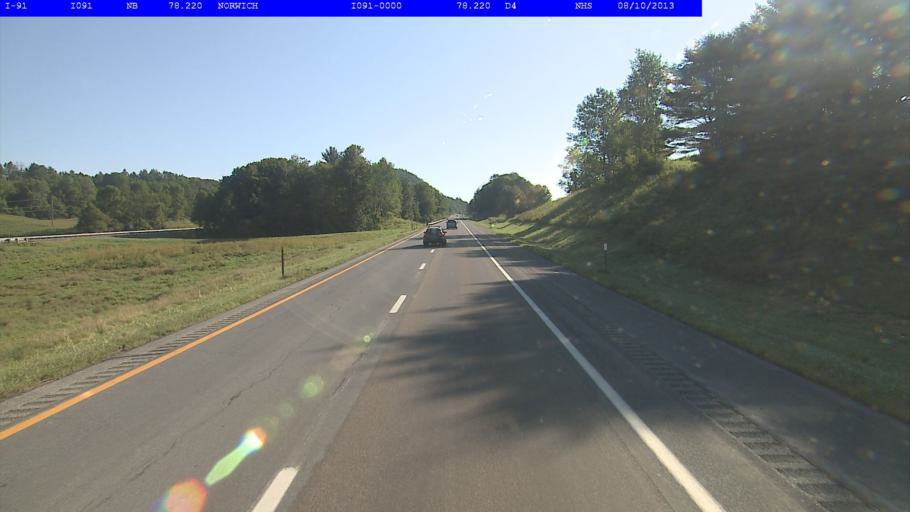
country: US
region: New Hampshire
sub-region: Grafton County
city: Hanover
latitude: 43.7428
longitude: -72.2633
